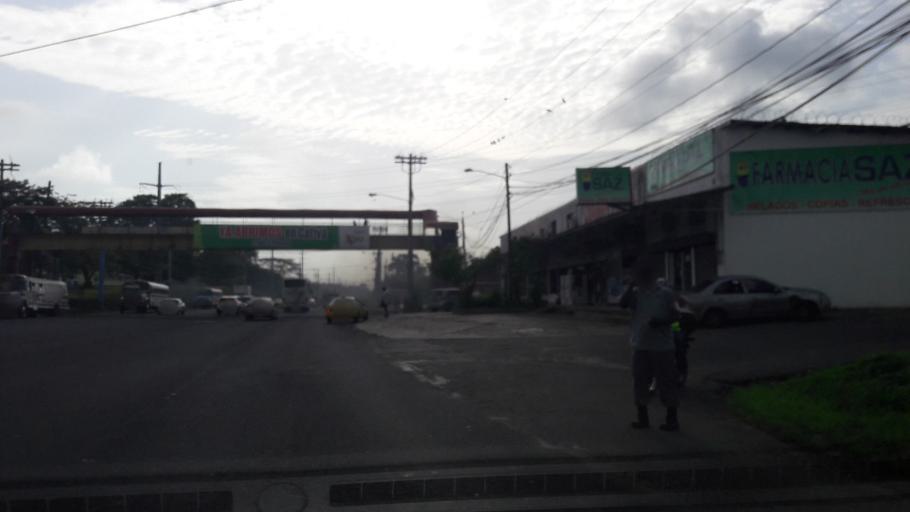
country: PA
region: Colon
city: Cativa
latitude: 9.3491
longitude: -79.8597
